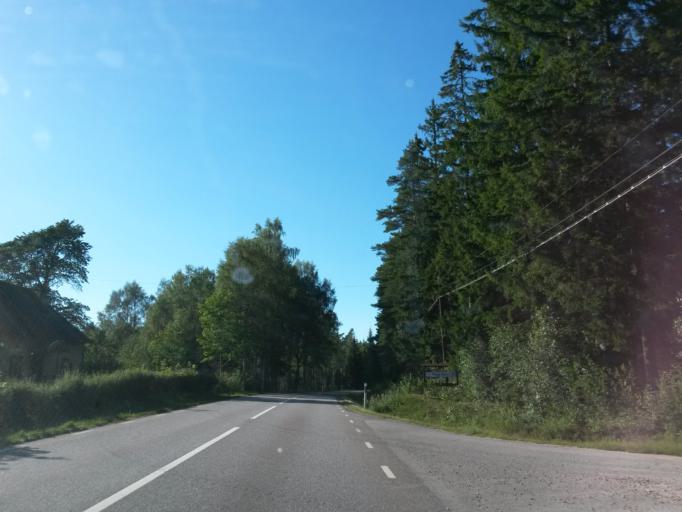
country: SE
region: Vaestra Goetaland
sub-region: Boras Kommun
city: Boras
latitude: 57.8507
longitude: 12.9478
